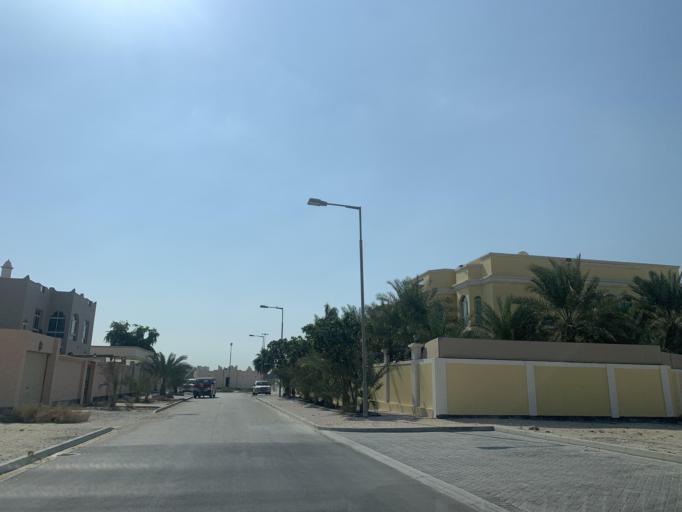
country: BH
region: Central Governorate
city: Madinat Hamad
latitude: 26.1136
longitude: 50.4947
